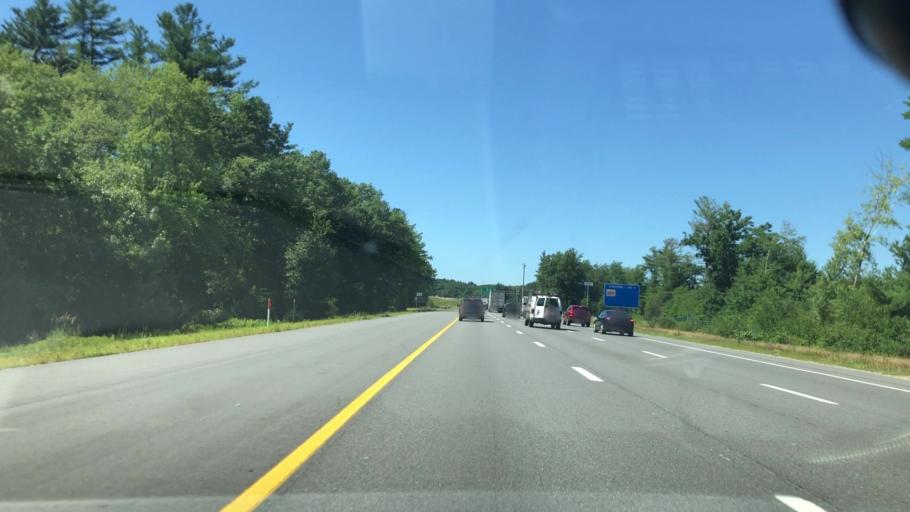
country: US
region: New Hampshire
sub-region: Rockingham County
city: Salem
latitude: 42.7707
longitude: -71.2400
